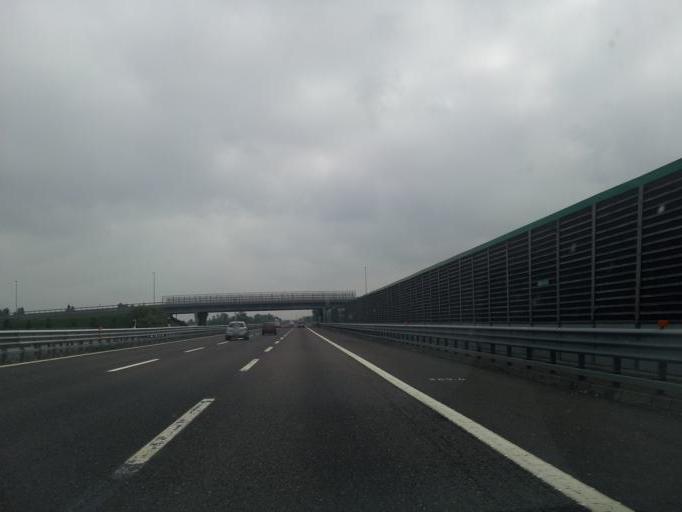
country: IT
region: Veneto
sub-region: Provincia di Padova
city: Ronchi di Campanile
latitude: 45.4611
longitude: 11.7748
